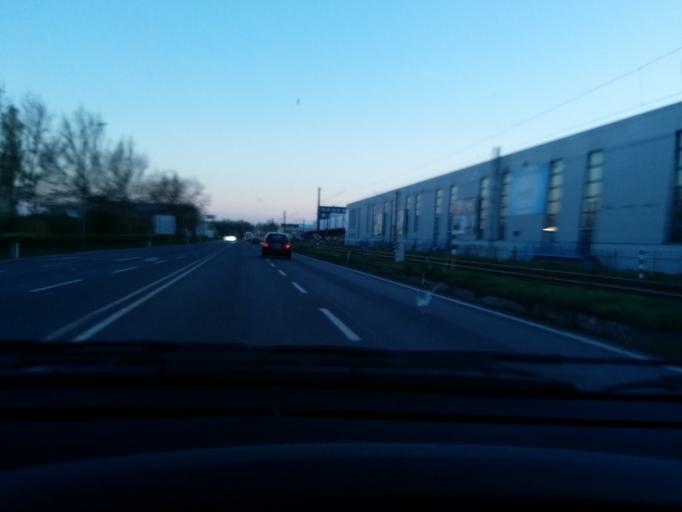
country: AT
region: Lower Austria
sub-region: Politischer Bezirk Modling
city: Wiener Neudorf
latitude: 48.0769
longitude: 16.3126
